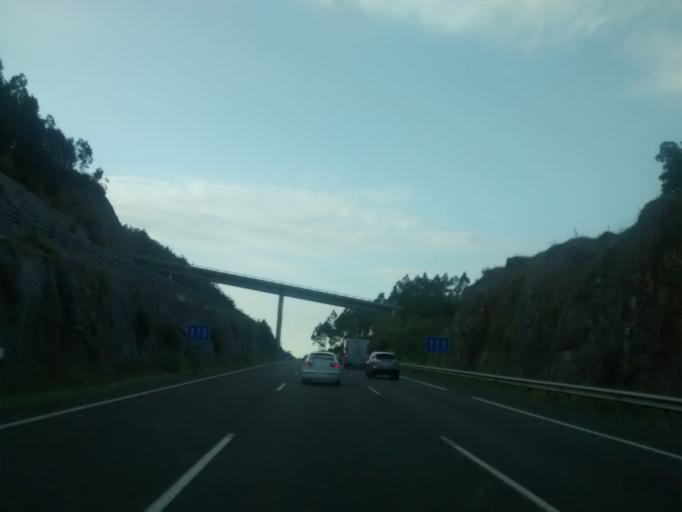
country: ES
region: Cantabria
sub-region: Provincia de Cantabria
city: Los Corrales de Buelna
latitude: 43.2933
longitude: -4.0778
